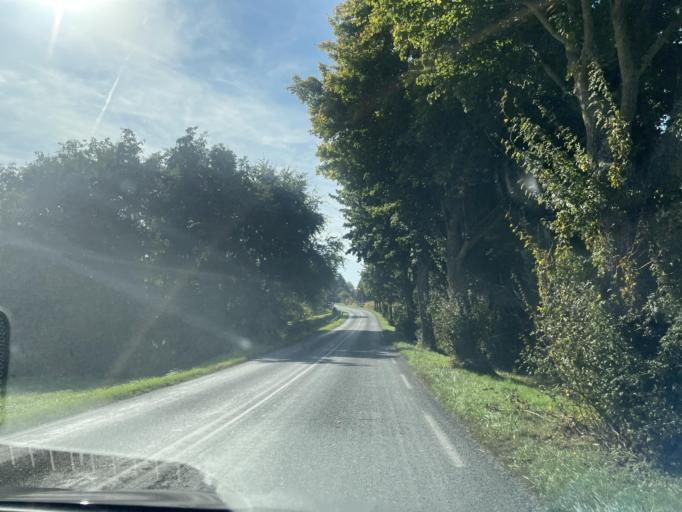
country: FR
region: Ile-de-France
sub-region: Departement de Seine-et-Marne
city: Coulommiers
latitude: 48.8430
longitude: 3.0881
